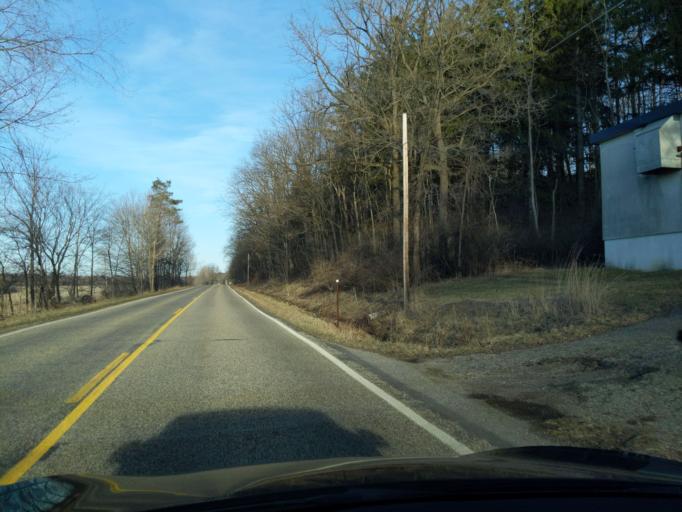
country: US
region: Michigan
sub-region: Ionia County
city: Ionia
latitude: 42.9644
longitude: -85.0879
